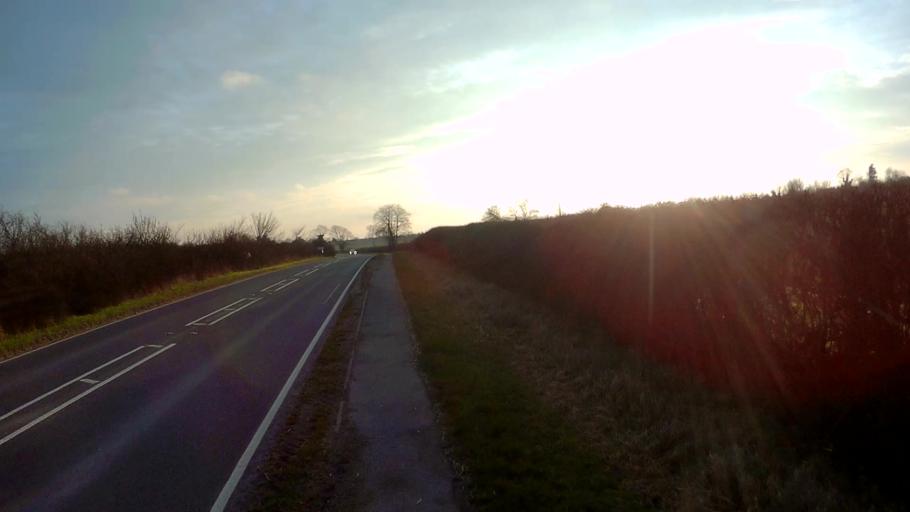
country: GB
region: England
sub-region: Lincolnshire
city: Bourne
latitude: 52.7864
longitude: -0.3767
